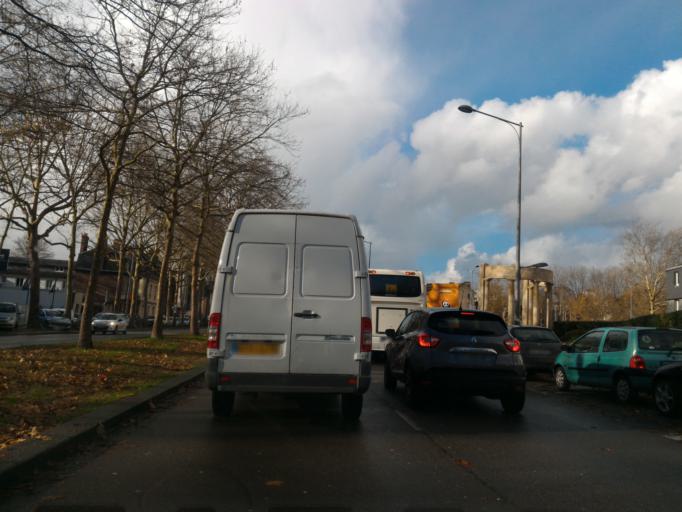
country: FR
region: Haute-Normandie
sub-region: Departement de la Seine-Maritime
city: Rouen
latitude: 49.4459
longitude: 1.1080
